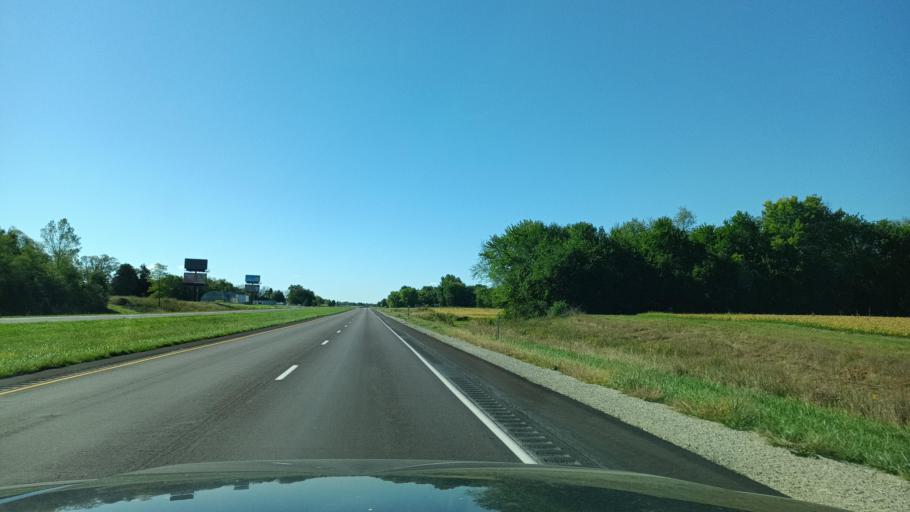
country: US
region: Illinois
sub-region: Hancock County
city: Nauvoo
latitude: 40.4772
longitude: -91.4446
